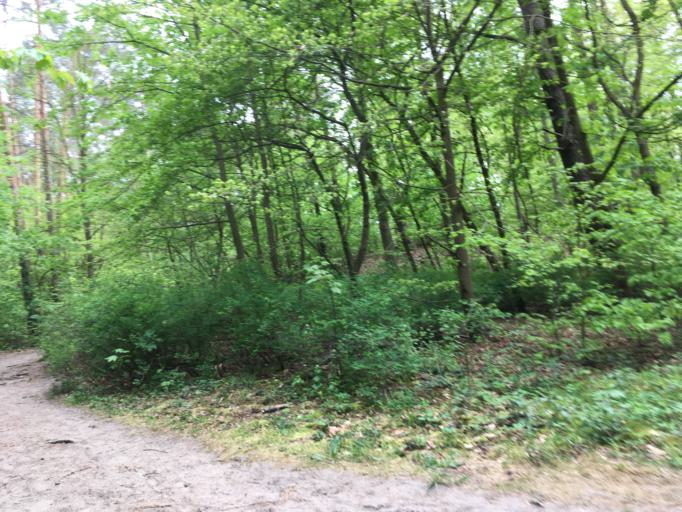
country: DE
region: Brandenburg
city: Rudnitz
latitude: 52.7309
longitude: 13.5975
